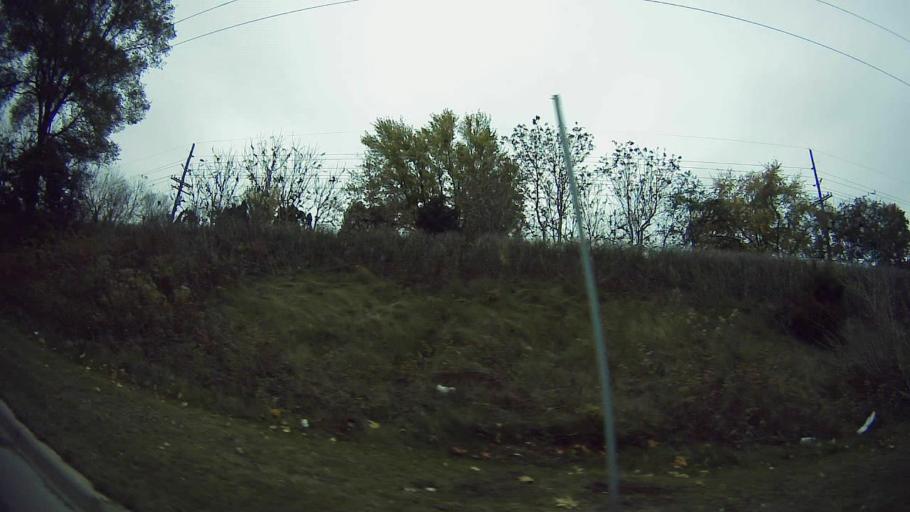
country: US
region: Michigan
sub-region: Oakland County
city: Waterford
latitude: 42.6780
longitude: -83.3654
